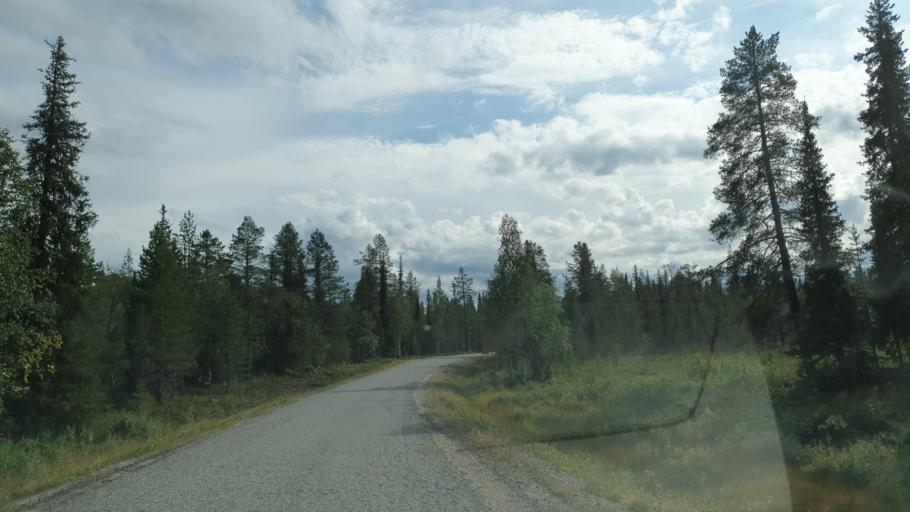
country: FI
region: Lapland
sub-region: Tunturi-Lappi
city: Kolari
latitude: 67.6867
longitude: 24.1112
